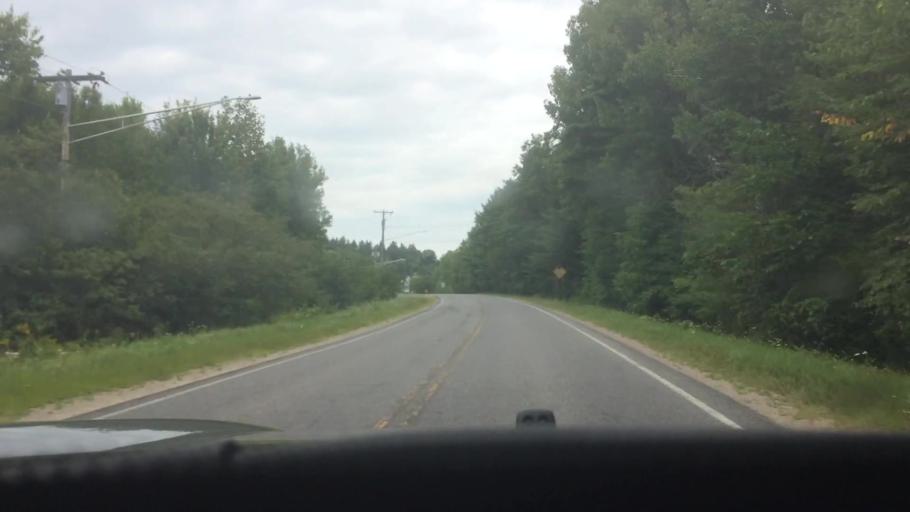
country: US
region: New York
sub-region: St. Lawrence County
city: Hannawa Falls
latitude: 44.5497
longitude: -74.9302
